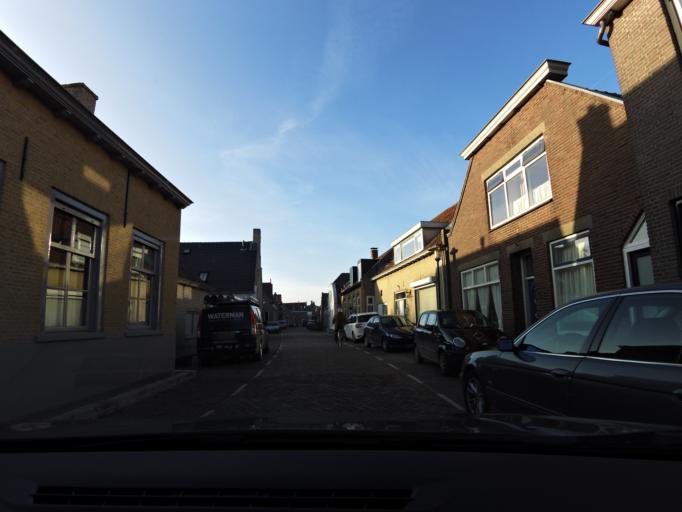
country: NL
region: South Holland
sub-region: Gemeente Dordrecht
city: Dordrecht
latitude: 51.7128
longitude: 4.6984
